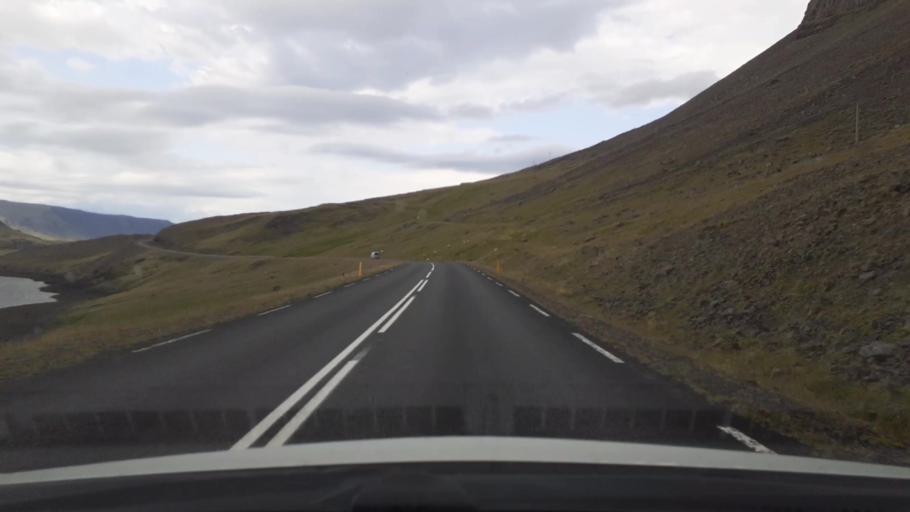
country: IS
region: Capital Region
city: Mosfellsbaer
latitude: 64.3887
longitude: -21.3979
